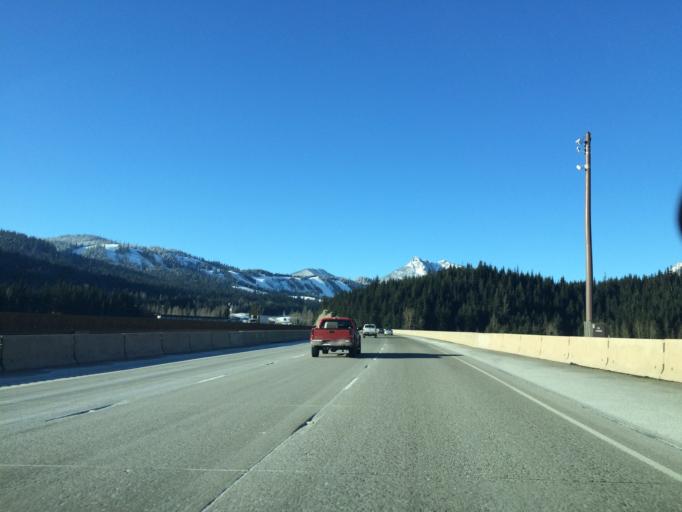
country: US
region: Washington
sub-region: King County
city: Tanner
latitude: 47.3897
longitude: -121.3817
